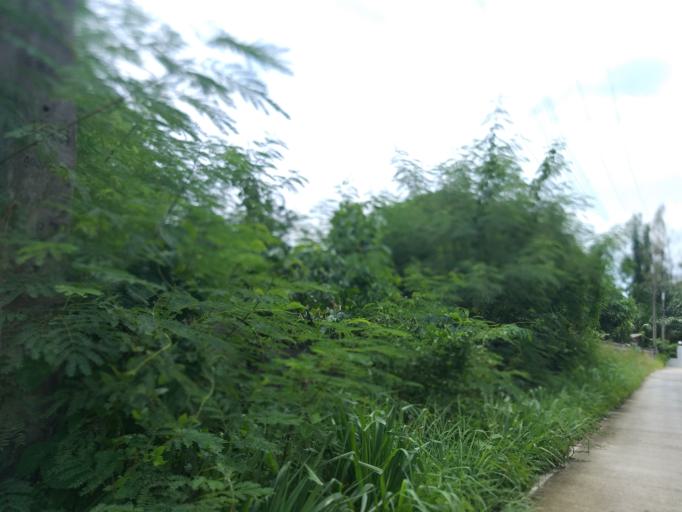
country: TH
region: Pathum Thani
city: Ban Lam Luk Ka
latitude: 13.9895
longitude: 100.8540
